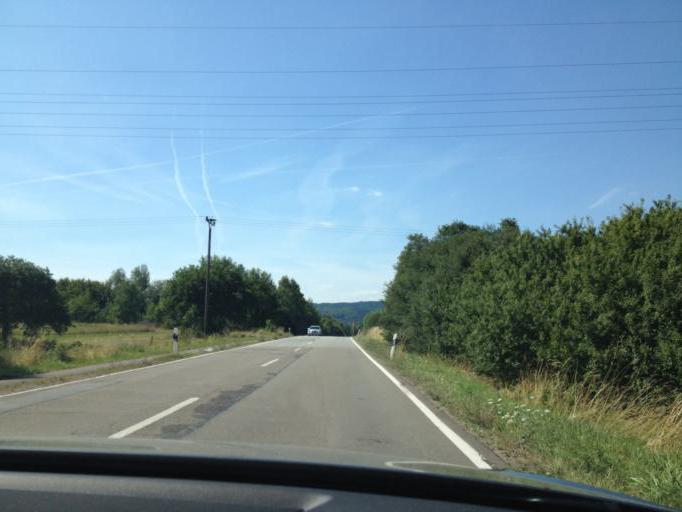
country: DE
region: Saarland
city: Oberthal
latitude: 49.5036
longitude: 7.1009
